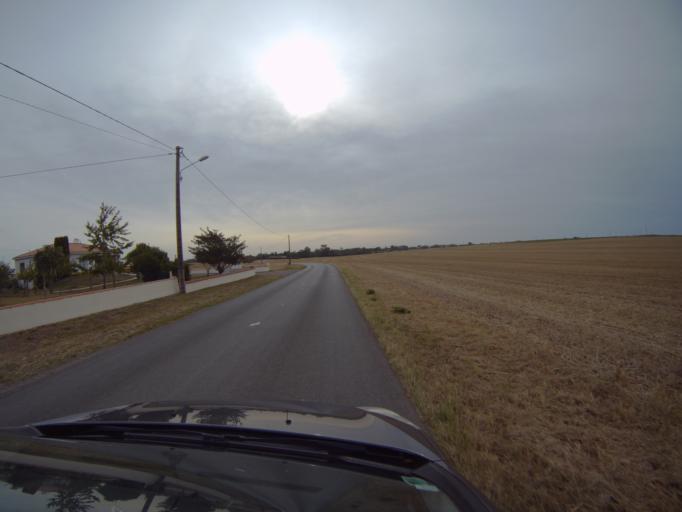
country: FR
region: Pays de la Loire
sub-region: Departement de la Vendee
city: Angles
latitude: 46.4069
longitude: -1.4297
